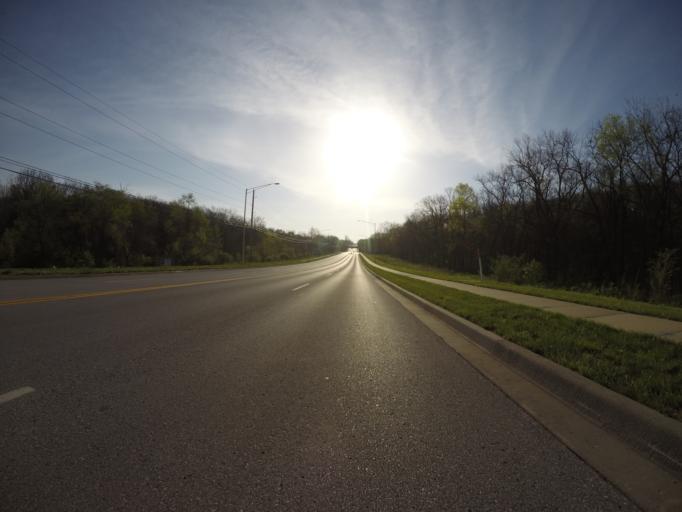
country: US
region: Missouri
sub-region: Jackson County
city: Lees Summit
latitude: 38.9121
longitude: -94.4233
